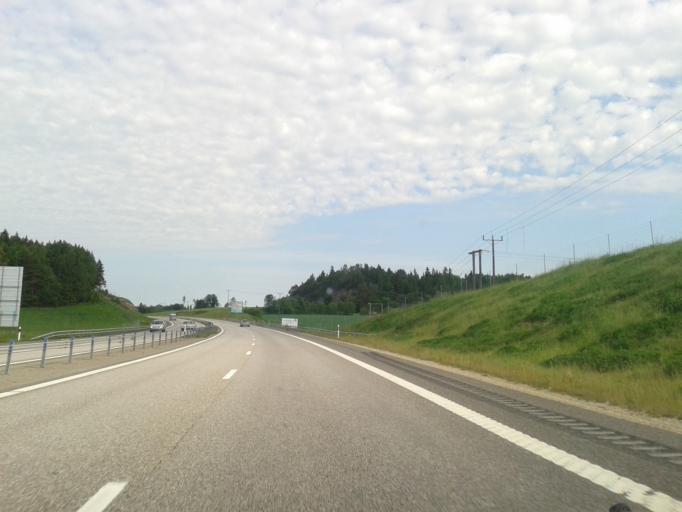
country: SE
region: Vaestra Goetaland
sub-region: Munkedals Kommun
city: Munkedal
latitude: 58.4717
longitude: 11.6485
